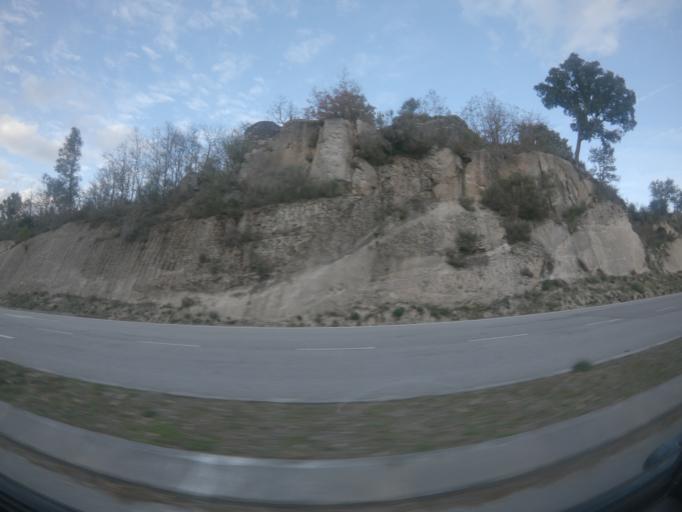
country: PT
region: Braganca
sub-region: Carrazeda de Ansiaes
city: Carrazeda de Anciaes
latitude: 41.2614
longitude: -7.3234
